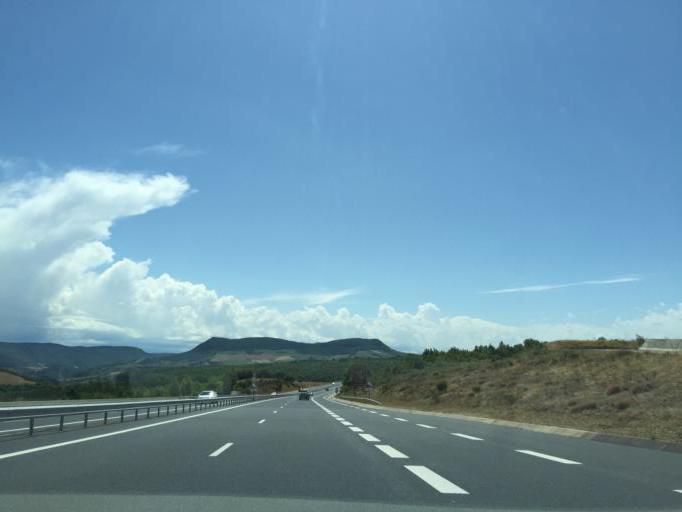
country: FR
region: Midi-Pyrenees
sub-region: Departement de l'Aveyron
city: Millau
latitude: 44.2053
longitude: 3.0673
